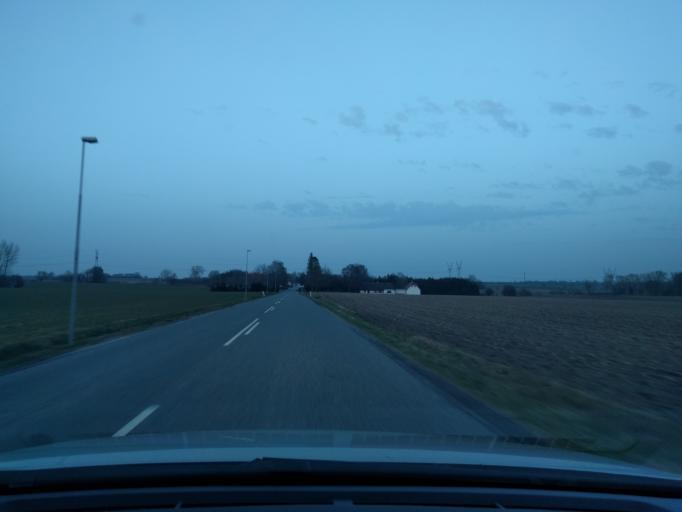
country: DK
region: South Denmark
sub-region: Odense Kommune
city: Bellinge
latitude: 55.3534
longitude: 10.2960
